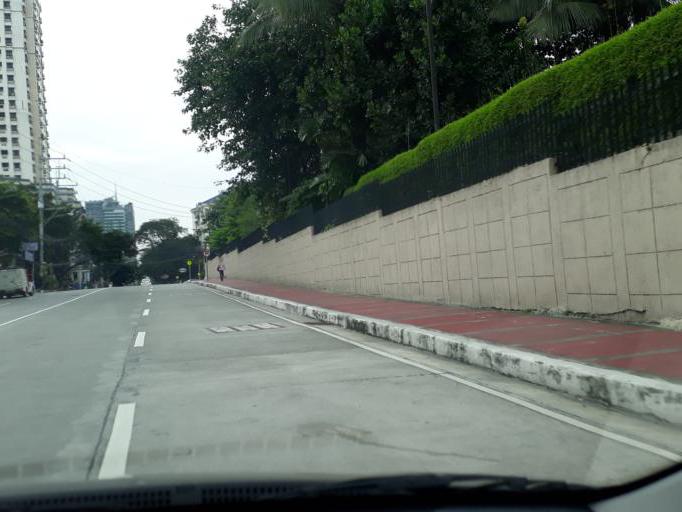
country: PH
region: Metro Manila
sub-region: Quezon City
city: Quezon City
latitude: 14.6394
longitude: 121.0377
